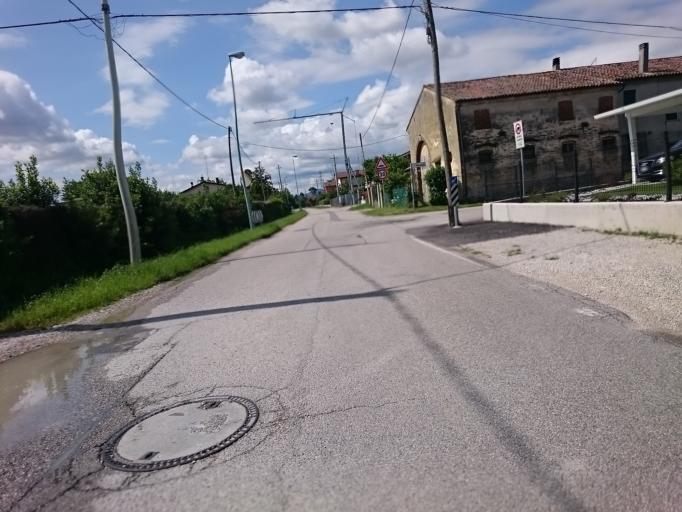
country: IT
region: Veneto
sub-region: Provincia di Padova
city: Rubano
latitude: 45.4363
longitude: 11.7831
